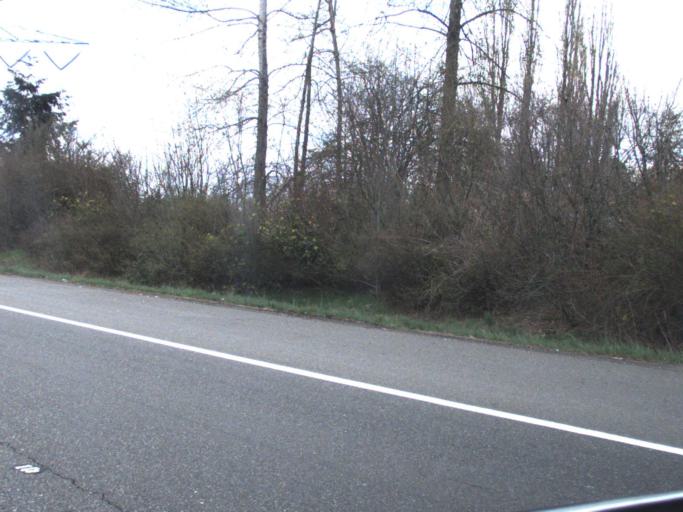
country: US
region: Washington
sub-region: King County
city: Covington
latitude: 47.3428
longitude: -122.1463
